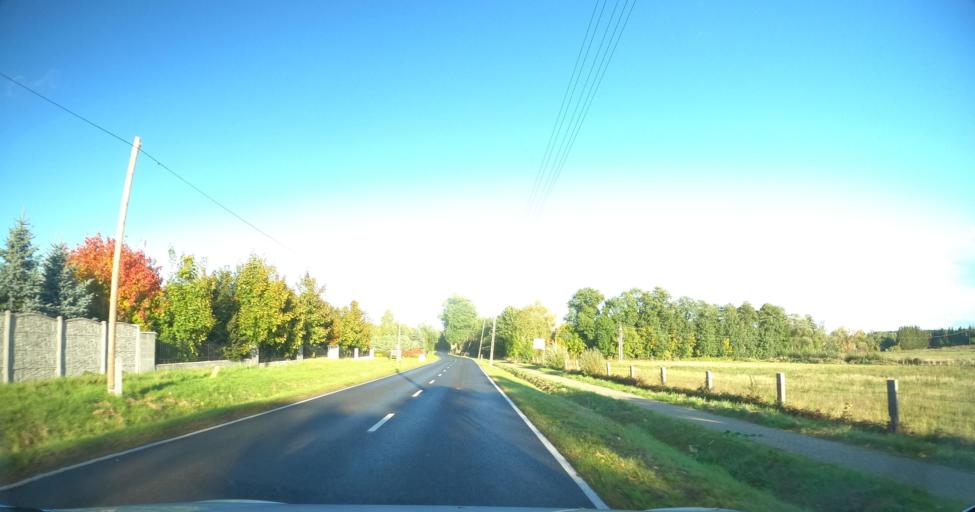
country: PL
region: Lubusz
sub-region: Powiat zielonogorski
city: Zabor
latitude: 51.9301
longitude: 15.6560
